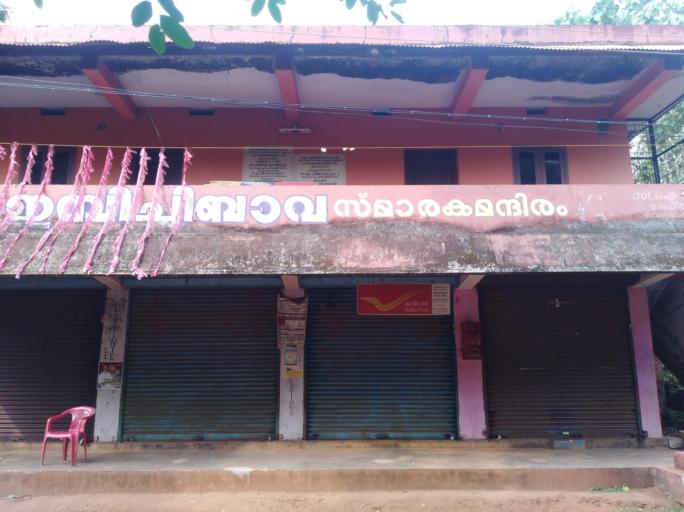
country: IN
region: Kerala
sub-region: Malappuram
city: Tirur
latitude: 10.8487
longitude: 76.0080
